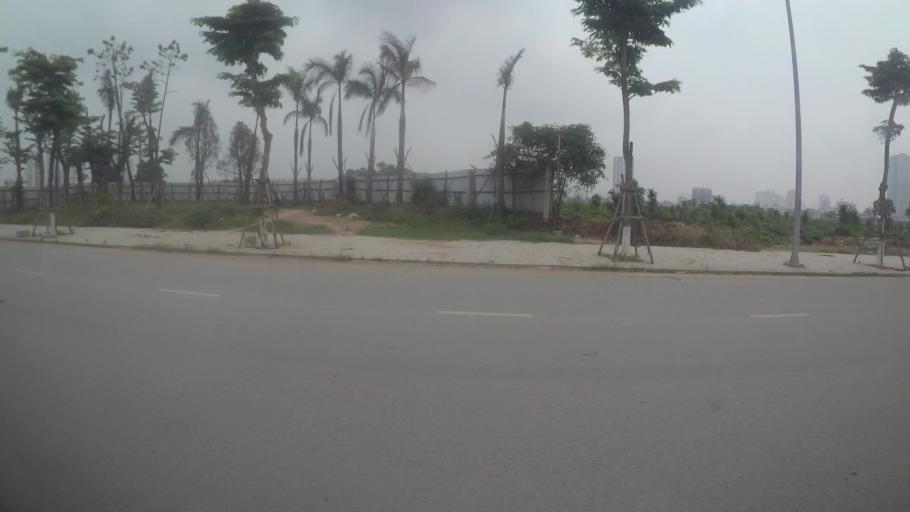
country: VN
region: Ha Noi
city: Ha Dong
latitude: 20.9816
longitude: 105.7591
